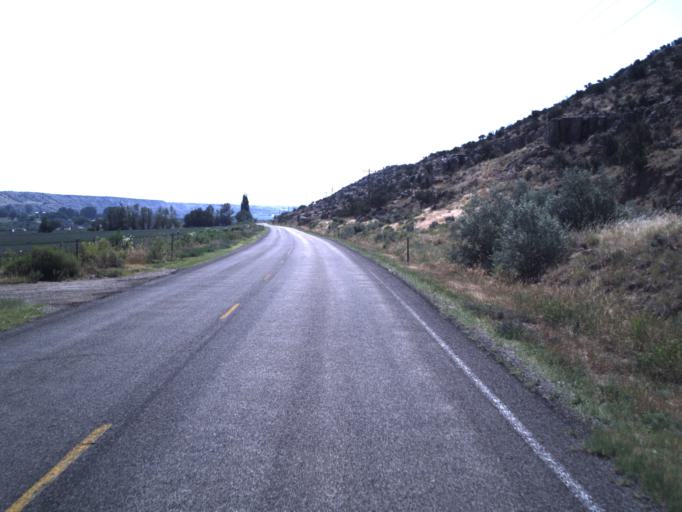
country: US
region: Utah
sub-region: Duchesne County
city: Duchesne
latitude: 40.2736
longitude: -110.4574
